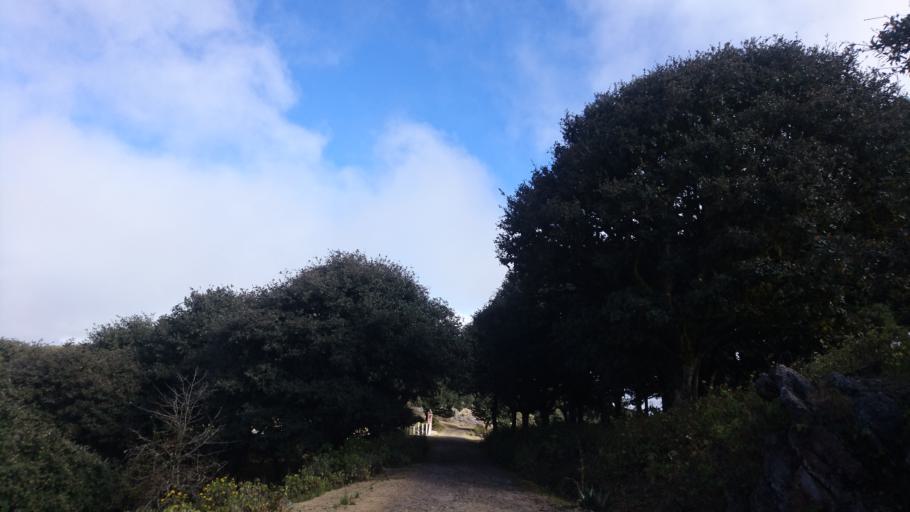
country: MX
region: San Luis Potosi
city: Zaragoza
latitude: 22.0681
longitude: -100.6464
